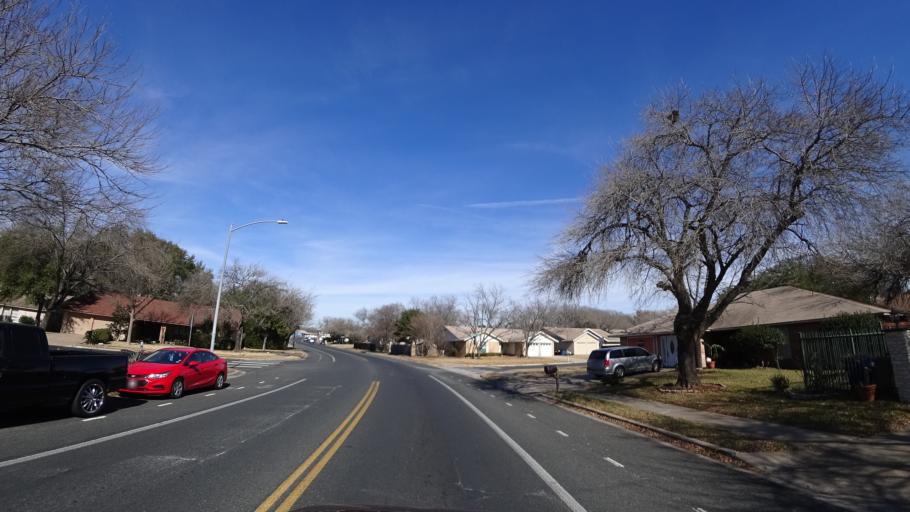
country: US
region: Texas
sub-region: Travis County
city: Wells Branch
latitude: 30.3806
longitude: -97.6982
